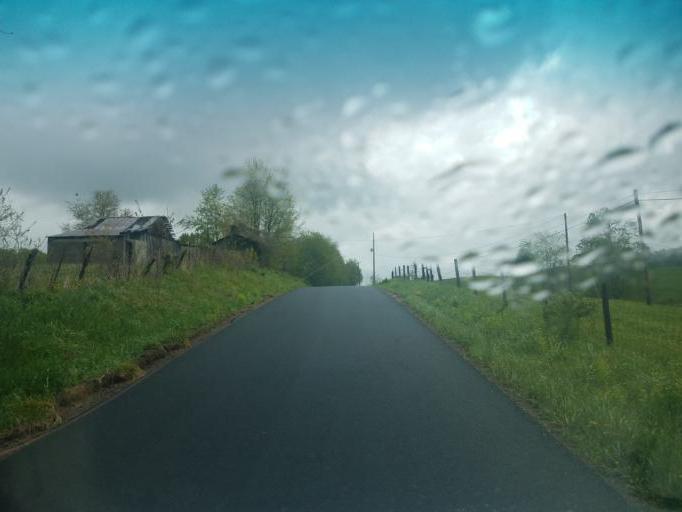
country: US
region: Virginia
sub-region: Smyth County
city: Marion
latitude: 36.9308
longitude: -81.5360
